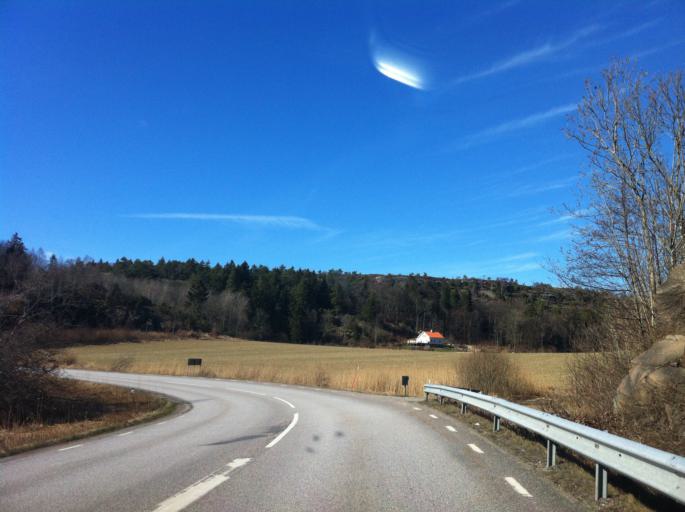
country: SE
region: Vaestra Goetaland
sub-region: Sotenas Kommun
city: Hunnebostrand
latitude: 58.4140
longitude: 11.3711
